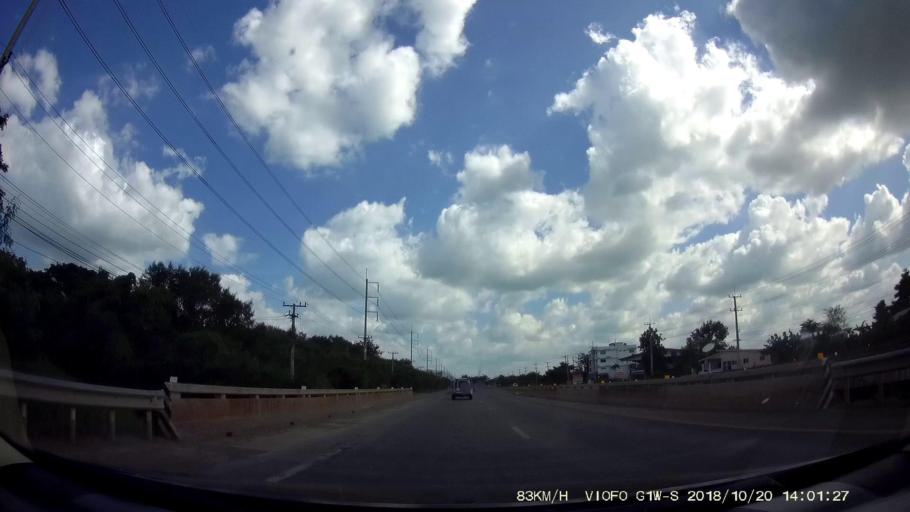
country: TH
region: Khon Kaen
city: Chum Phae
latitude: 16.5025
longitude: 102.1209
